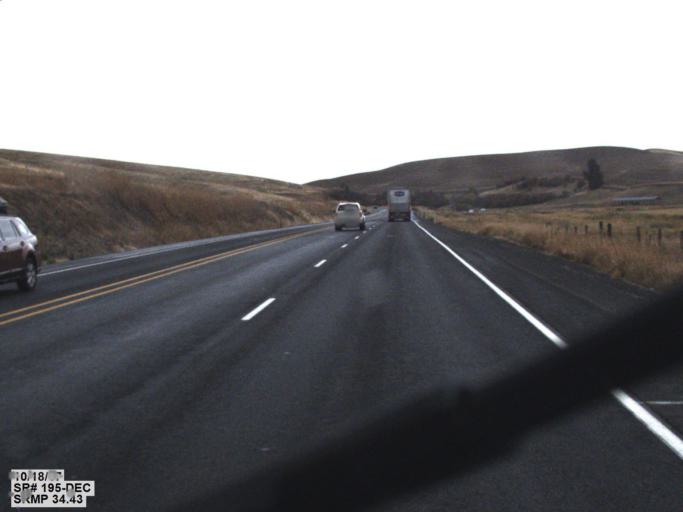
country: US
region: Washington
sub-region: Whitman County
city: Colfax
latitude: 46.8422
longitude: -117.3393
